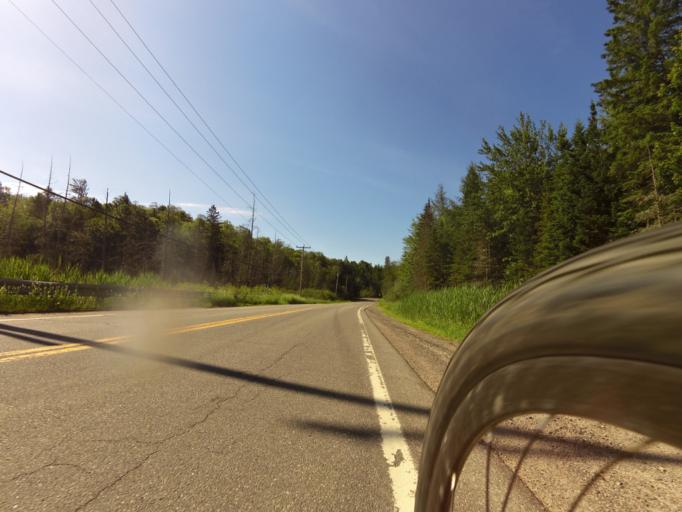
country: CA
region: Quebec
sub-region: Laurentides
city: Brownsburg-Chatham
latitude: 45.8449
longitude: -74.5568
